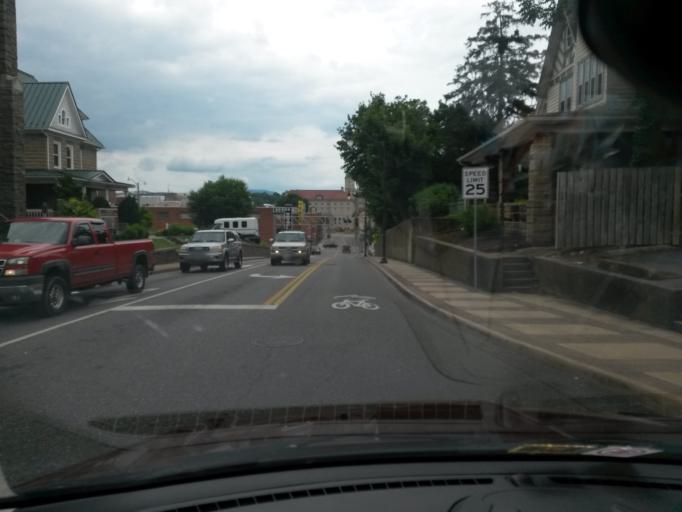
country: US
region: Virginia
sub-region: City of Harrisonburg
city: Harrisonburg
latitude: 38.4499
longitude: -78.8725
